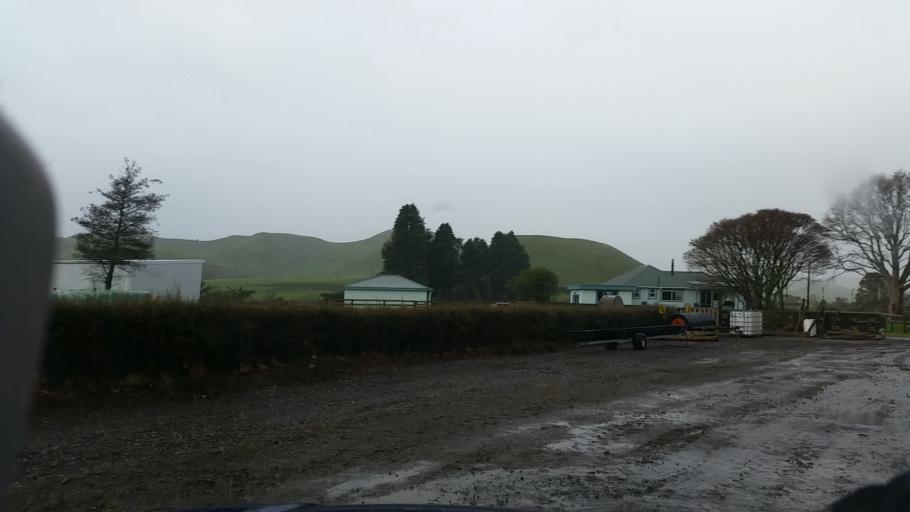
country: NZ
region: Taranaki
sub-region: South Taranaki District
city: Eltham
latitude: -39.3436
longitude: 174.4351
